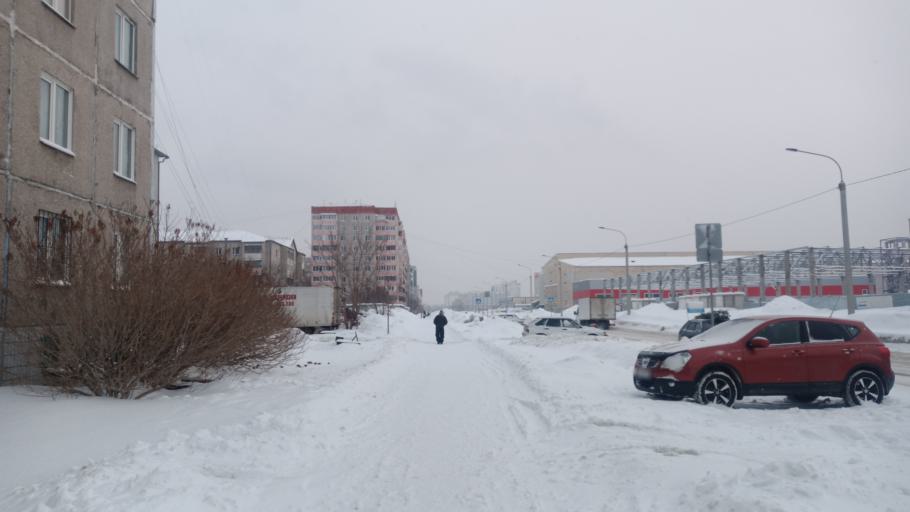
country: RU
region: Altai Krai
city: Novosilikatnyy
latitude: 53.3314
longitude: 83.6700
